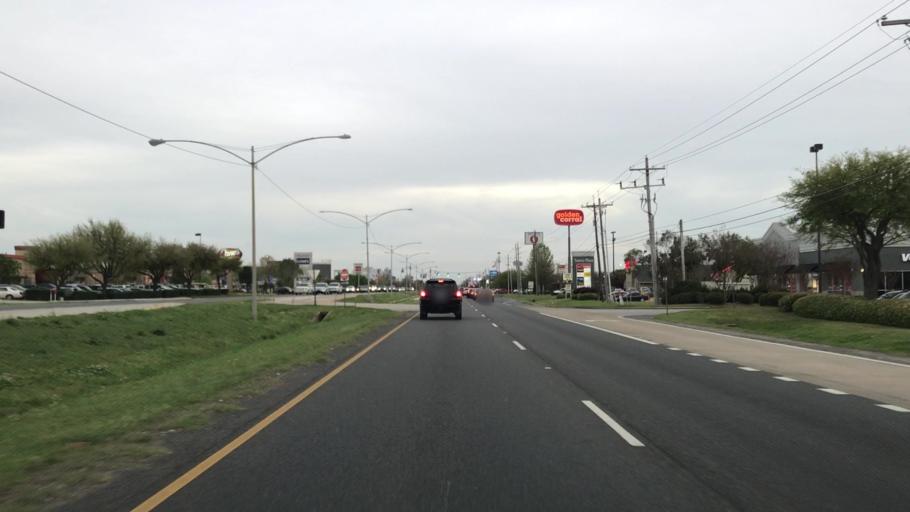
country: US
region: Louisiana
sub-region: Bossier Parish
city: Bossier City
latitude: 32.4406
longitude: -93.7171
